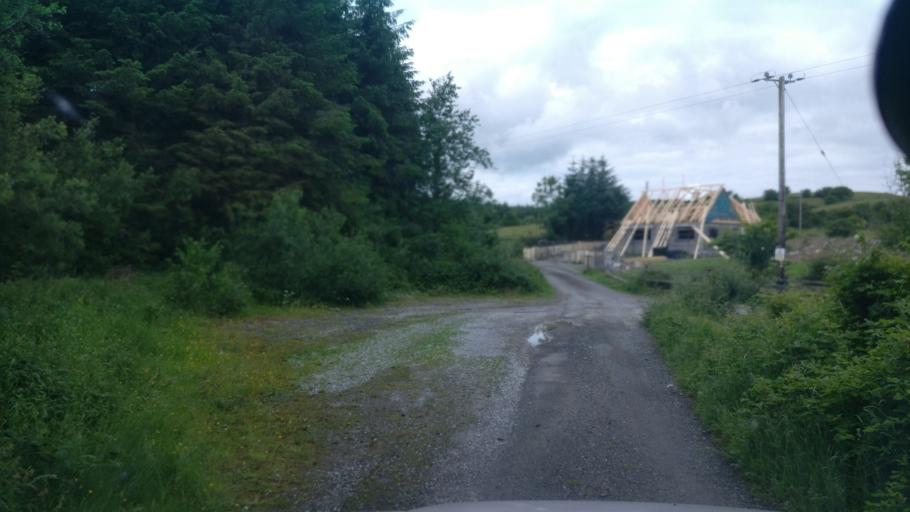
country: IE
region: Connaught
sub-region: County Galway
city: Loughrea
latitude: 53.1474
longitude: -8.5588
